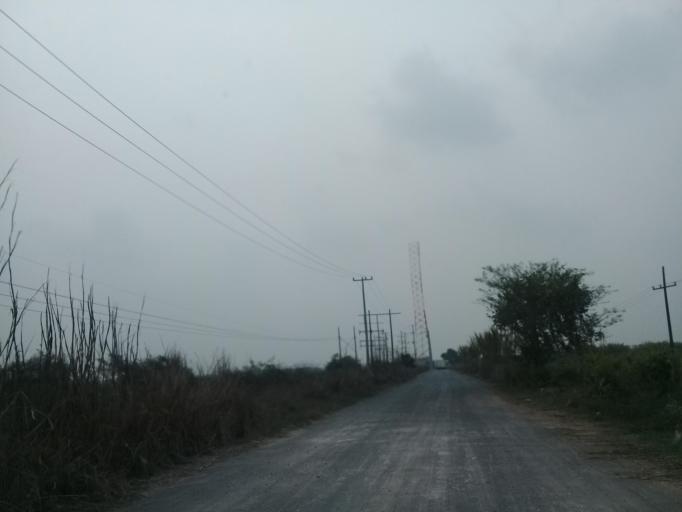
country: MX
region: Veracruz
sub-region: Medellin
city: La Laguna y Monte del Castillo
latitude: 18.9100
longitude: -96.1956
